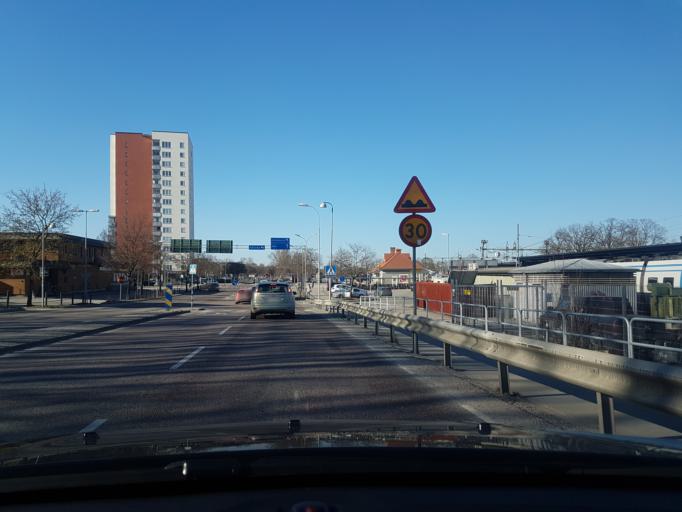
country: SE
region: Stockholm
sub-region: Sigtuna Kommun
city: Marsta
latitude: 59.6269
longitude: 17.8607
